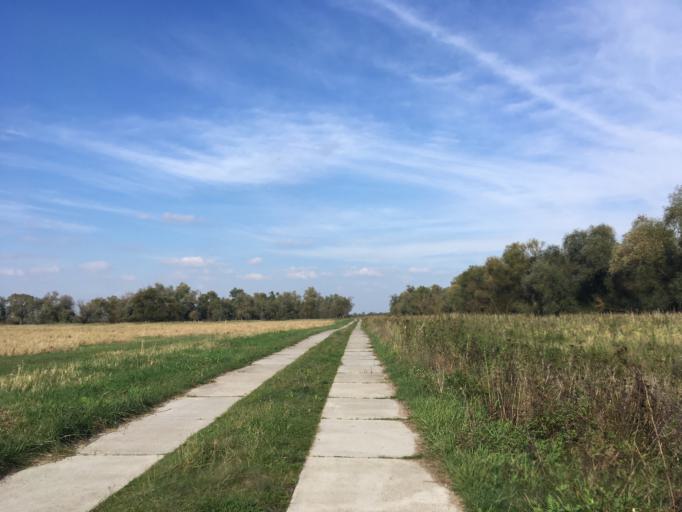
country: DE
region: Brandenburg
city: Schwedt (Oder)
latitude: 53.0209
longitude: 14.2758
